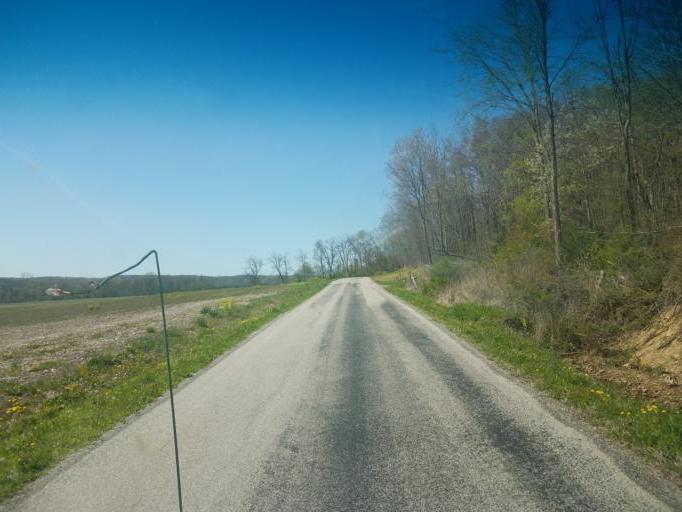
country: US
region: Ohio
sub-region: Medina County
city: Lodi
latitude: 40.9458
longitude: -82.0171
